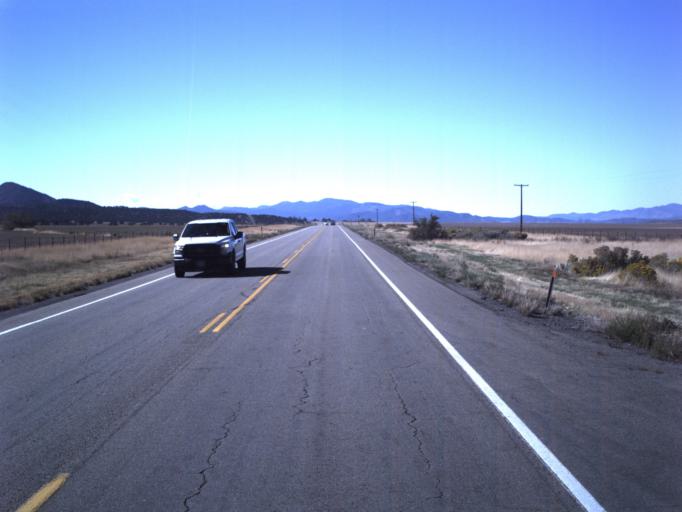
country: US
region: Utah
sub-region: Juab County
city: Nephi
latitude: 39.4679
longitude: -111.8981
